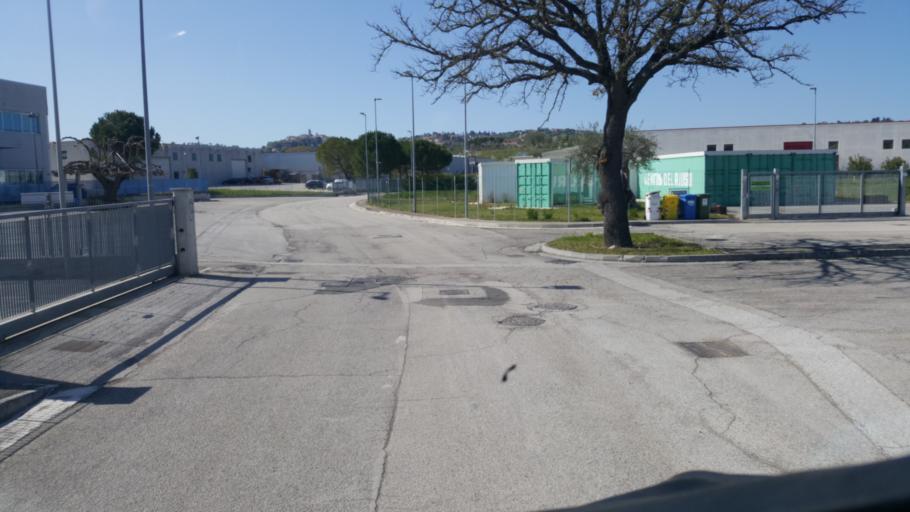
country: IT
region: The Marches
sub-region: Provincia di Macerata
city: Montecassiano
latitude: 43.3529
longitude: 13.4597
